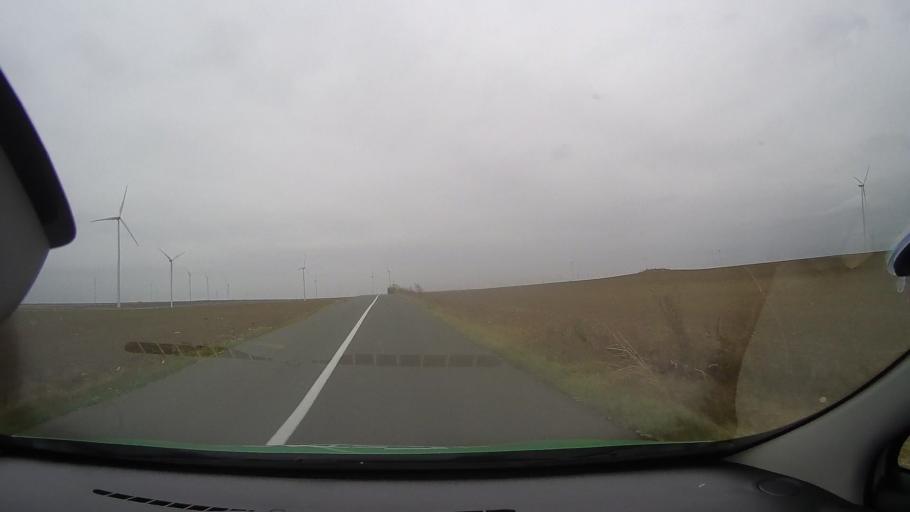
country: RO
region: Constanta
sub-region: Comuna Pantelimon
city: Pantelimon
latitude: 44.5089
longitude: 28.3417
